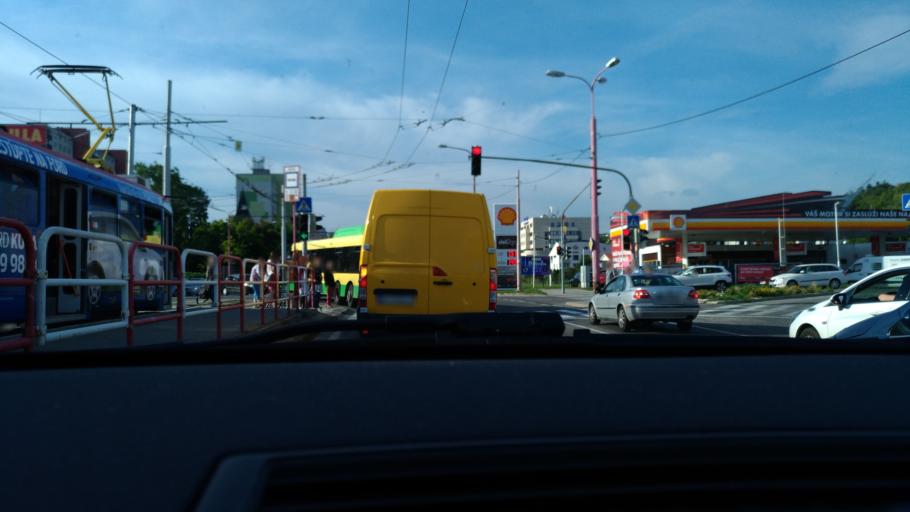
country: SK
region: Bratislavsky
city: Bratislava
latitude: 48.1497
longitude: 17.0631
